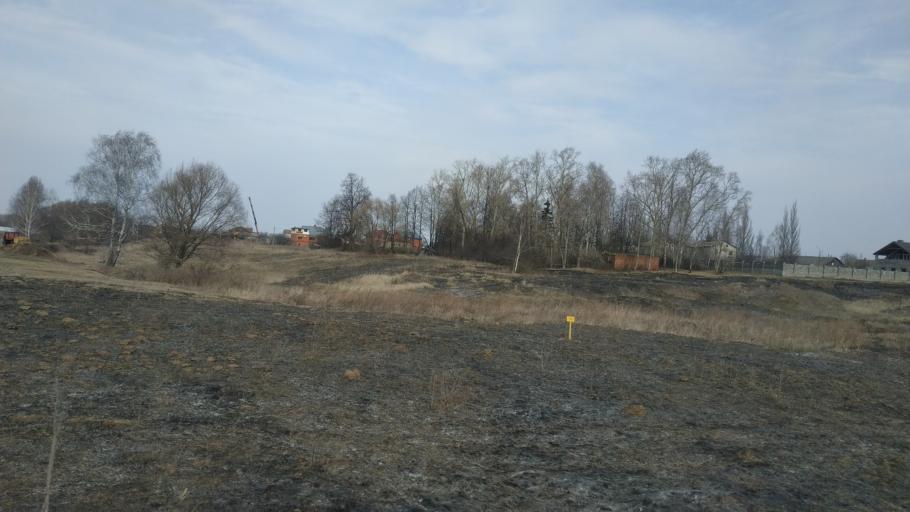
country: RU
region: Moskovskaya
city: Troitskoye
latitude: 55.3454
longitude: 38.5811
